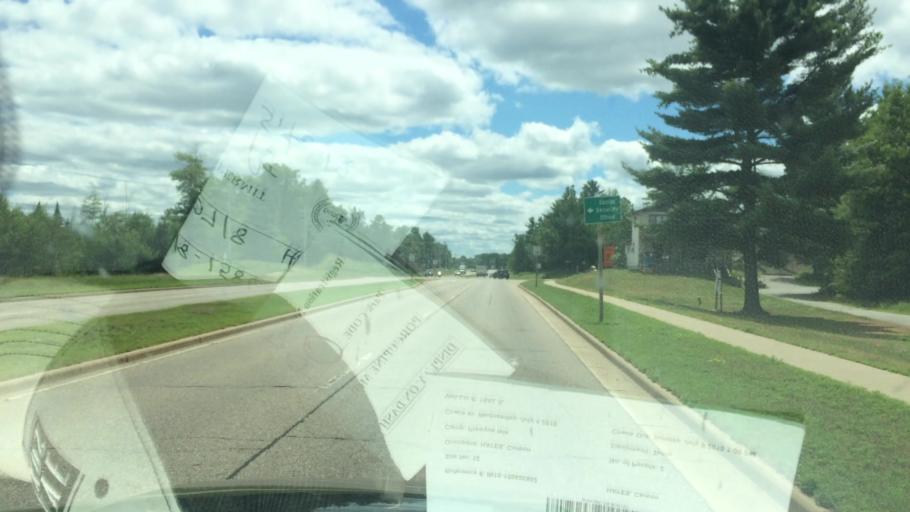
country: US
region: Wisconsin
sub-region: Oneida County
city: Rhinelander
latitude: 45.6526
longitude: -89.3818
